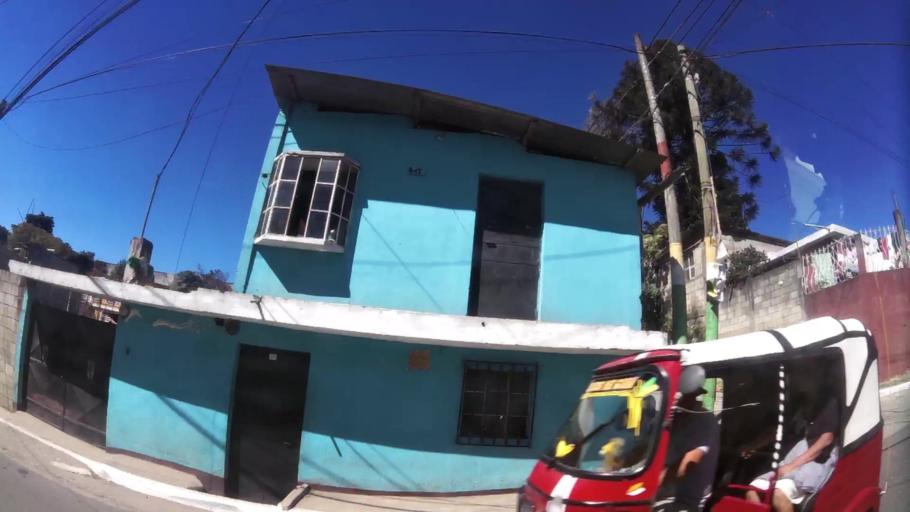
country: GT
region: Guatemala
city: San Jose Pinula
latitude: 14.5420
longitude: -90.4131
